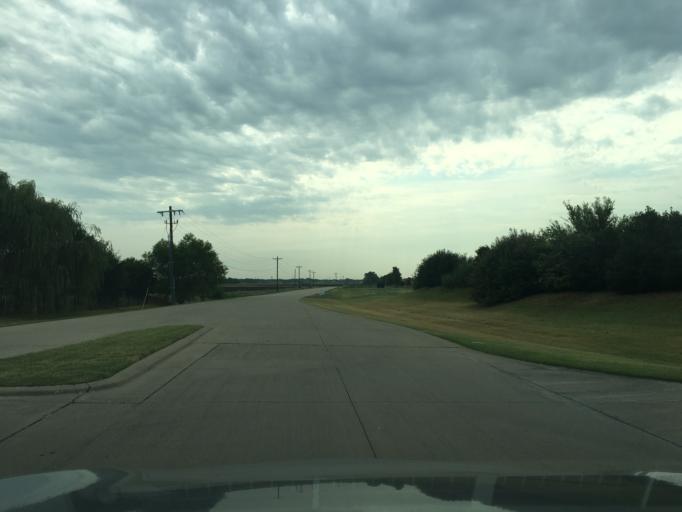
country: US
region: Texas
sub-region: Collin County
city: Parker
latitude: 33.0687
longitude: -96.6125
